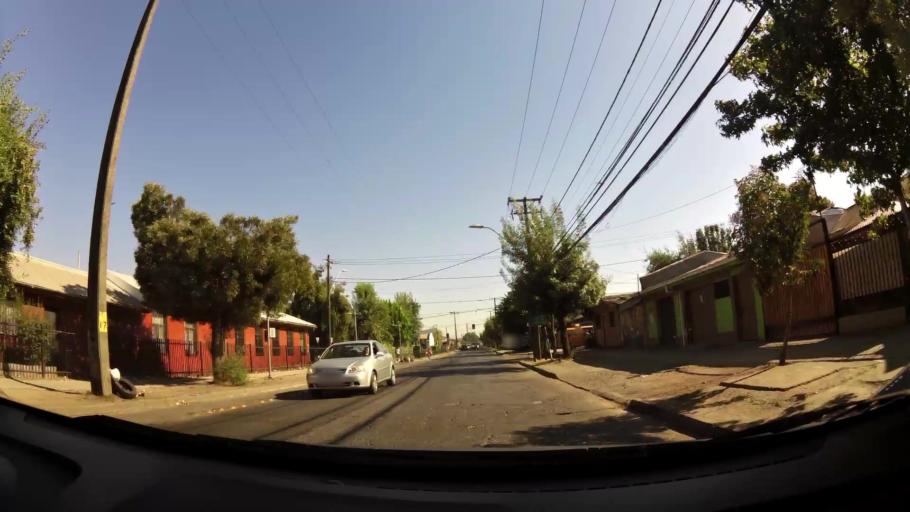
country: CL
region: Maule
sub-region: Provincia de Curico
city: Curico
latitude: -34.9915
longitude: -71.2484
